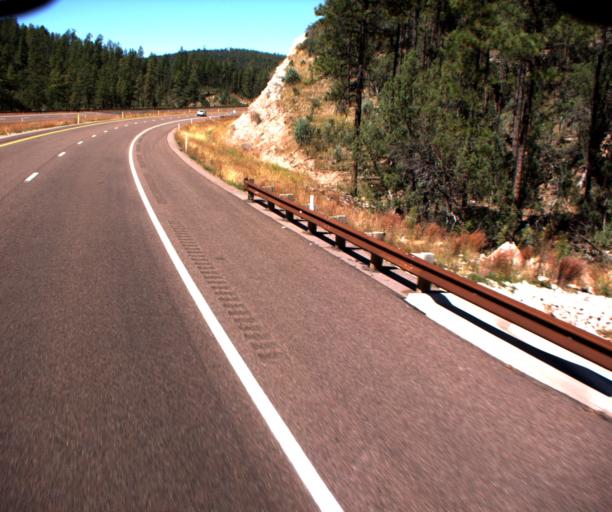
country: US
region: Arizona
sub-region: Gila County
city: Star Valley
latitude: 34.3246
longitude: -111.0838
